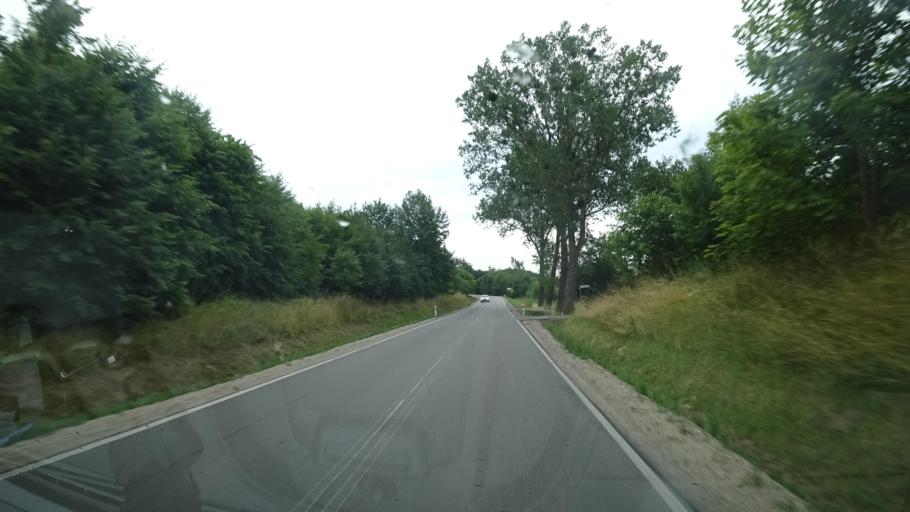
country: PL
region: Warmian-Masurian Voivodeship
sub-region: Powiat gizycki
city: Ryn
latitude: 53.9374
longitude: 21.5332
